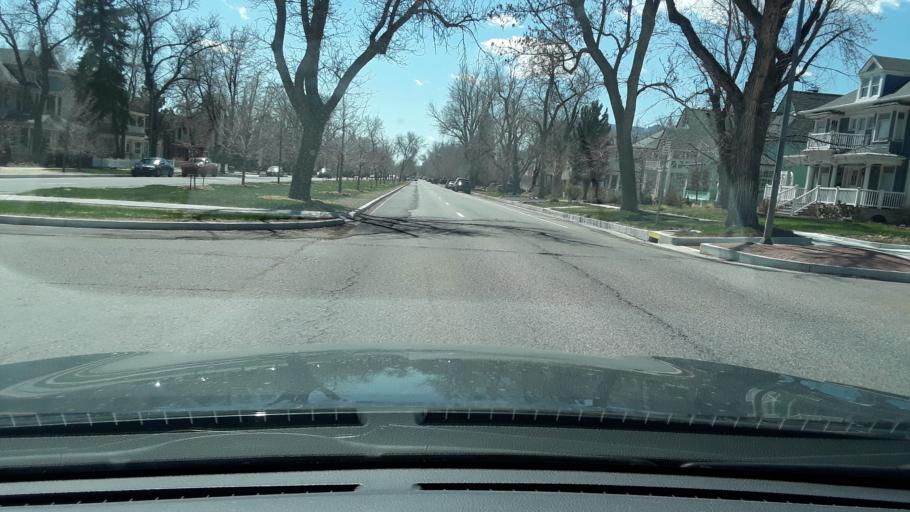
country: US
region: Colorado
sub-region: El Paso County
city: Colorado Springs
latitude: 38.8564
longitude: -104.8206
